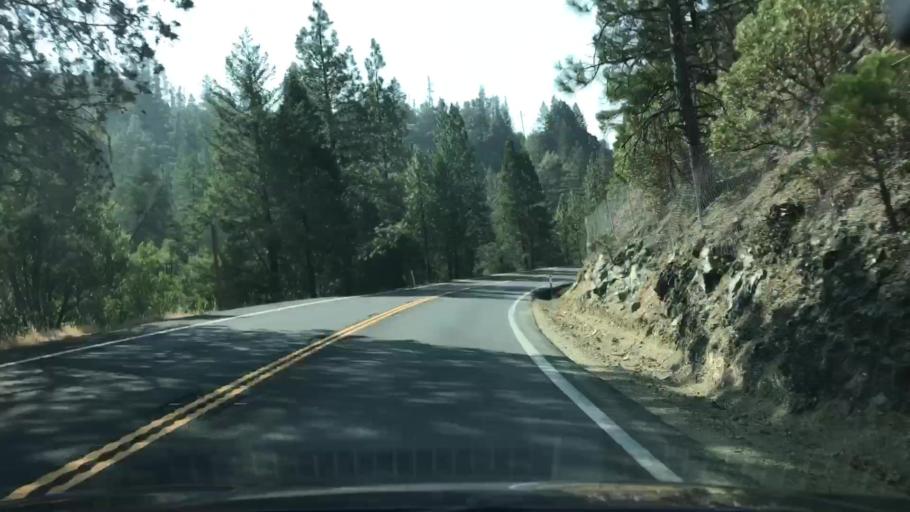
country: US
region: California
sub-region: Lake County
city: Middletown
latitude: 38.6801
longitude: -122.5906
